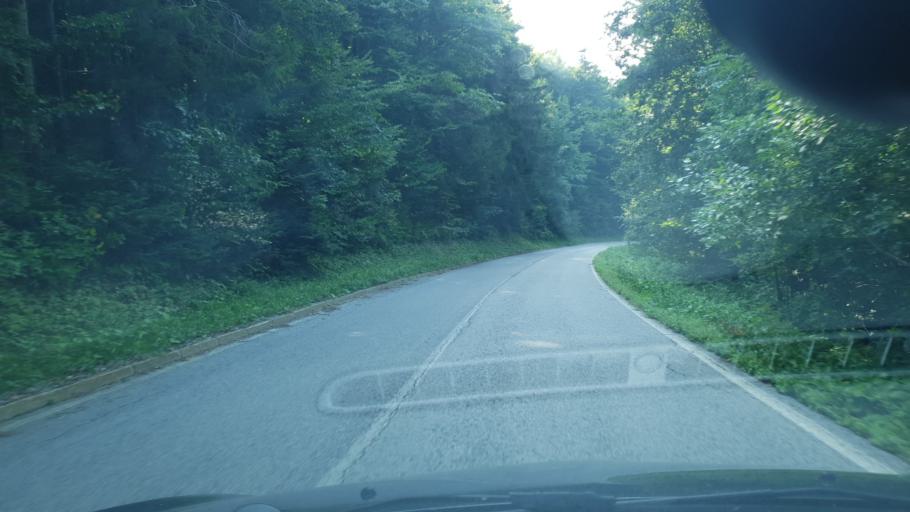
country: HR
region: Grad Zagreb
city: Kasina
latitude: 45.9087
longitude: 15.9761
